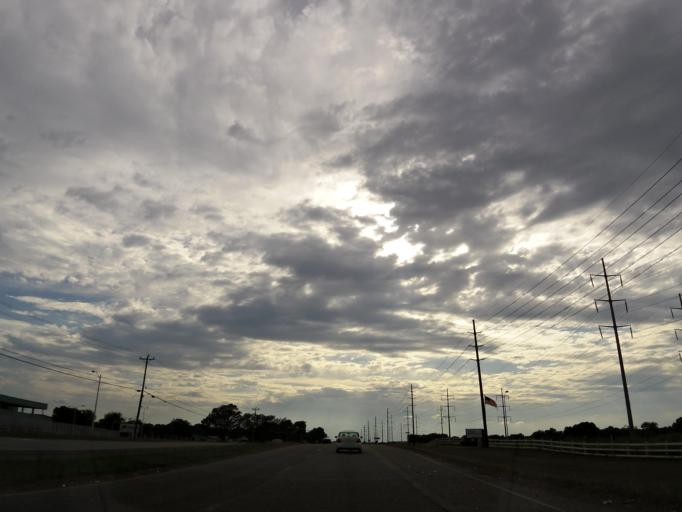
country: US
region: Alabama
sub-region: Morgan County
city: Decatur
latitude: 34.6193
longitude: -87.0166
